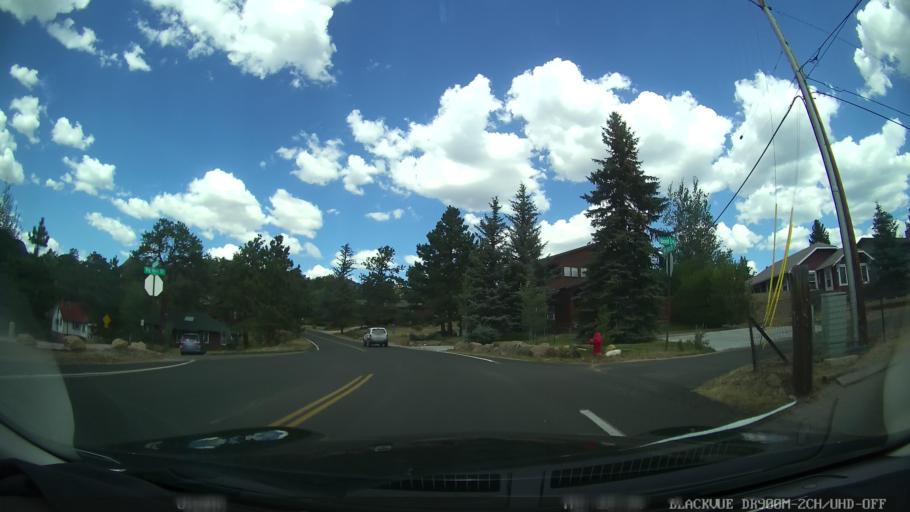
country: US
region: Colorado
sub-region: Larimer County
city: Estes Park
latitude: 40.3774
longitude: -105.5249
